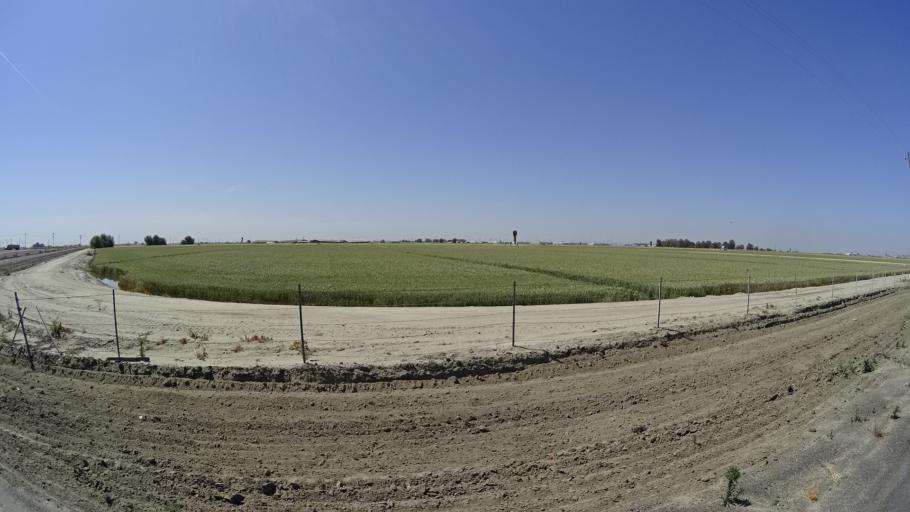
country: US
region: California
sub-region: Kings County
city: Corcoran
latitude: 36.0727
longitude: -119.5393
